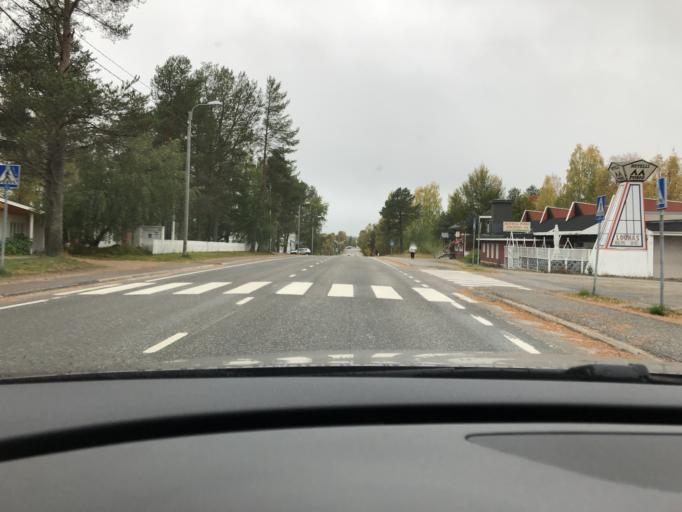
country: FI
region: Lapland
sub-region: Itae-Lappi
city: Posio
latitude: 66.1099
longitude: 28.1713
